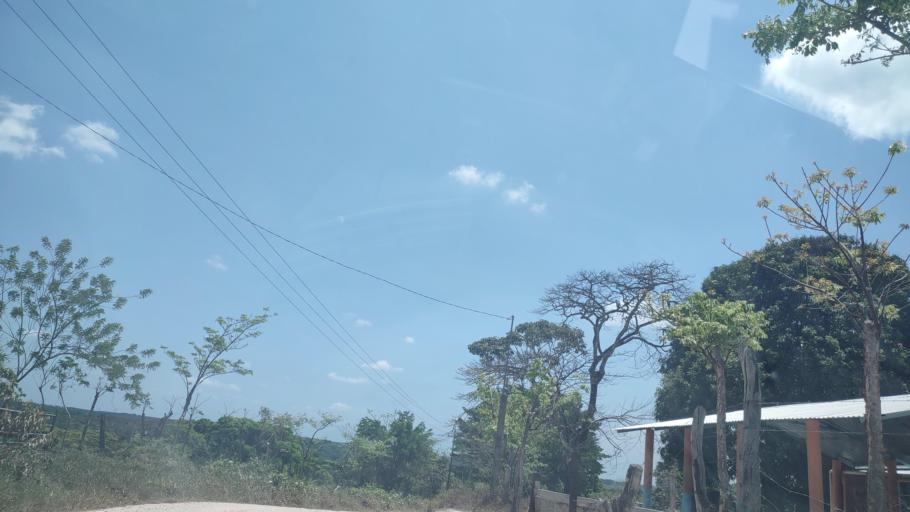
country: MX
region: Veracruz
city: Las Choapas
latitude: 17.7927
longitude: -94.1383
